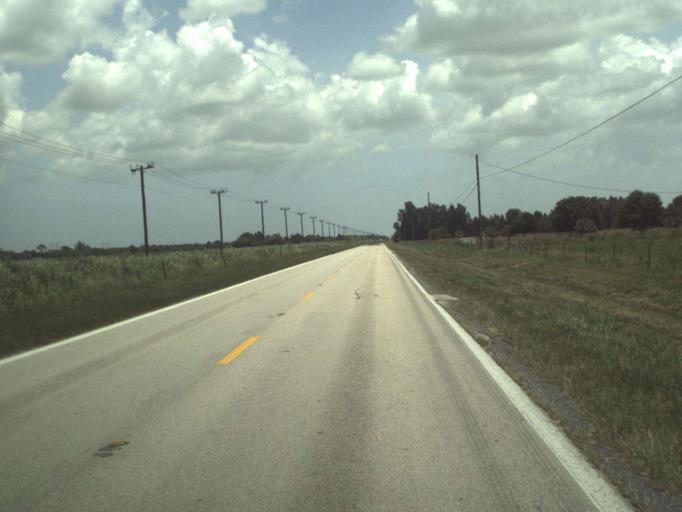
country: US
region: Florida
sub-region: Saint Lucie County
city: Fort Pierce South
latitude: 27.3744
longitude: -80.4707
